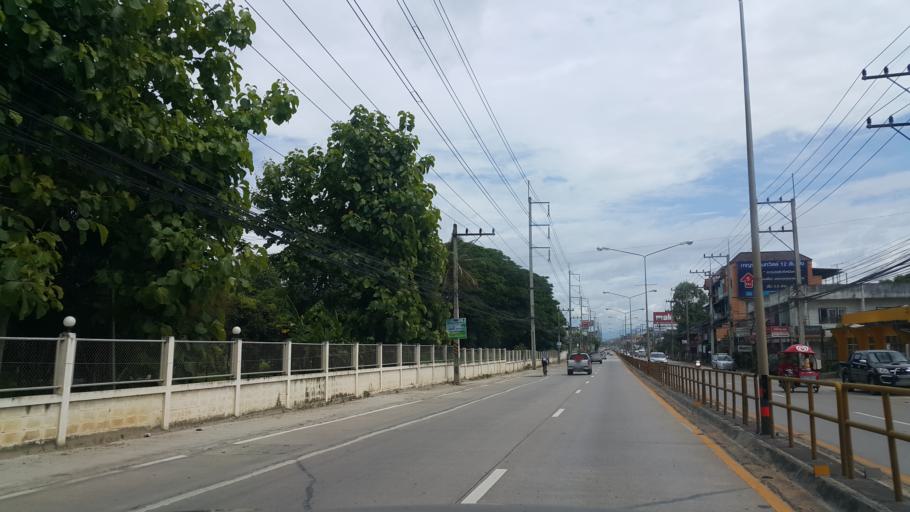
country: TH
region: Chiang Mai
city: San Sai
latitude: 18.8946
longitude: 98.9525
